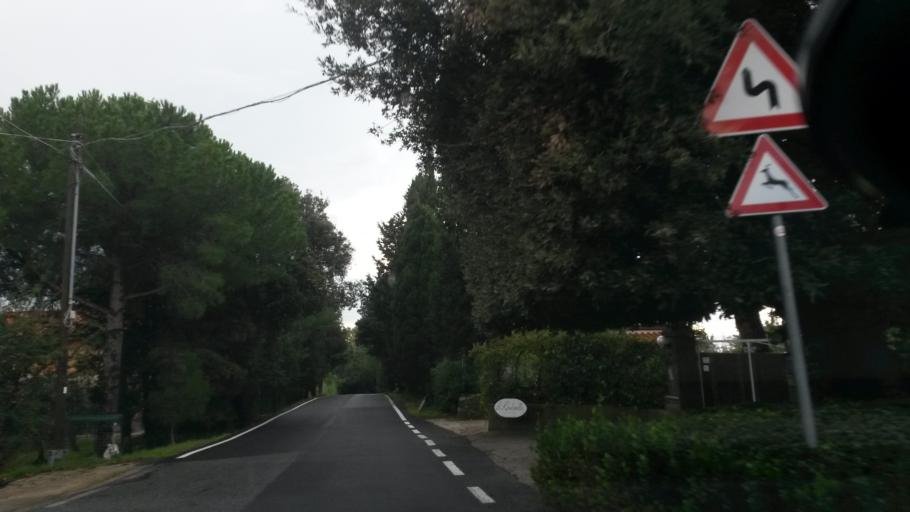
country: IT
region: Tuscany
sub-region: Provincia di Livorno
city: Rosignano Solvay-Castiglioncello
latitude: 43.4091
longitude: 10.4488
